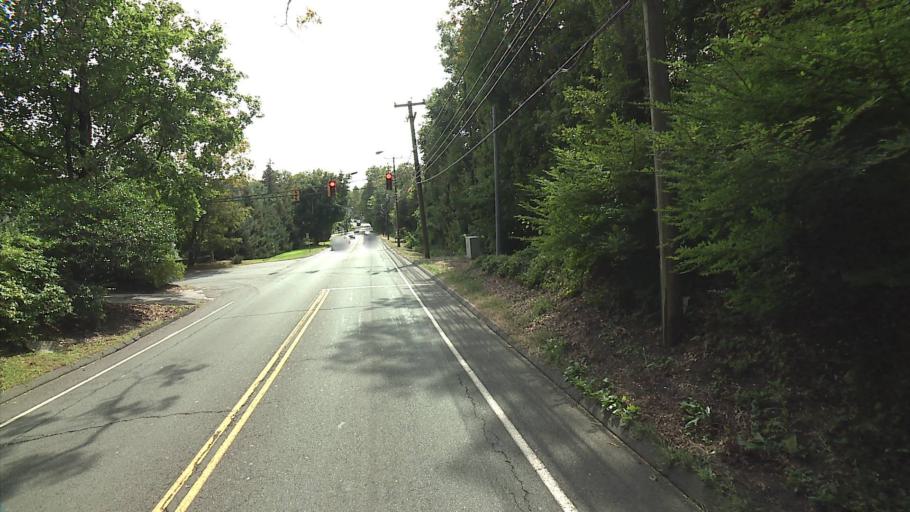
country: US
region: Connecticut
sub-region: Fairfield County
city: North Stamford
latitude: 41.1258
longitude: -73.5445
